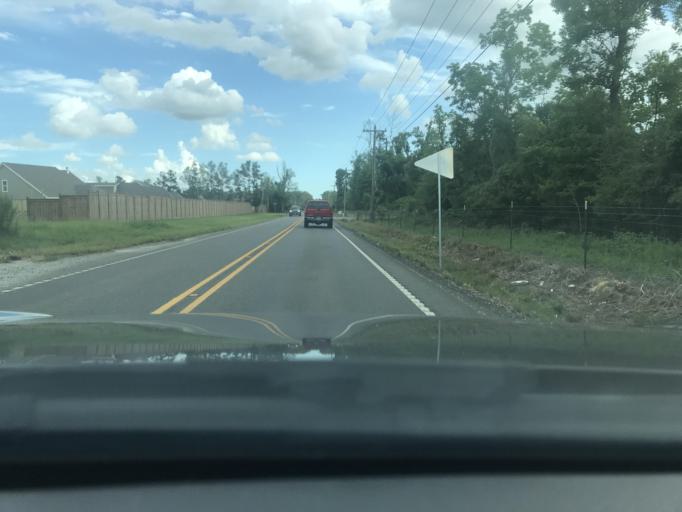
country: US
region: Louisiana
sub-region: Calcasieu Parish
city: Moss Bluff
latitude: 30.3144
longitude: -93.2583
